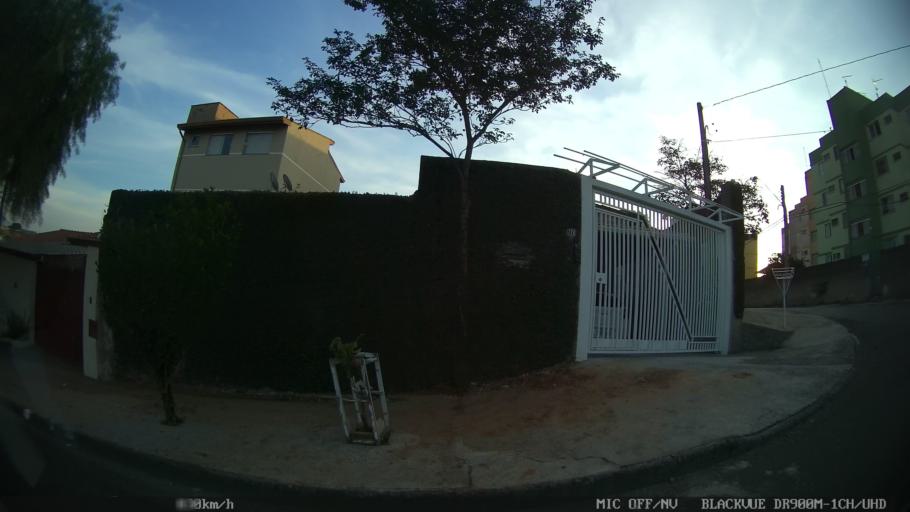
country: BR
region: Sao Paulo
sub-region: Campinas
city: Campinas
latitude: -22.9824
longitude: -47.1330
